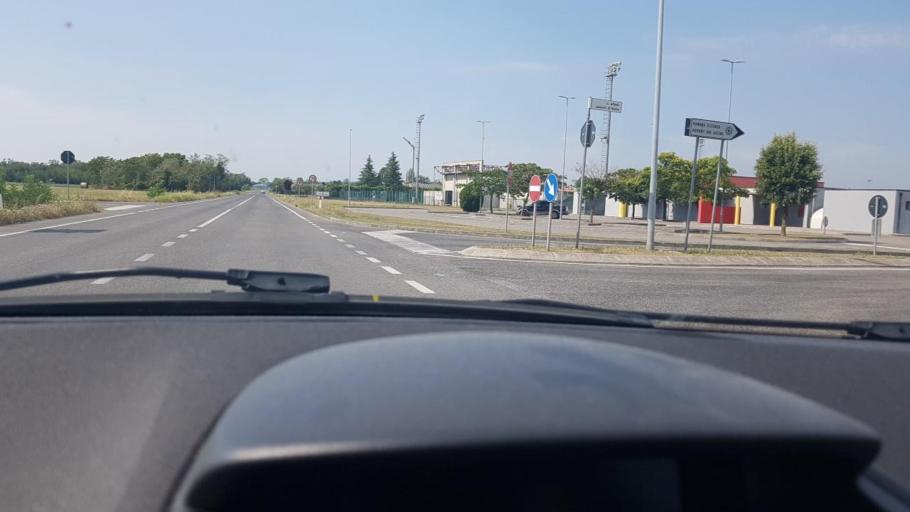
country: IT
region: Friuli Venezia Giulia
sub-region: Provincia di Gorizia
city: Romans d'Isonzo
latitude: 45.8889
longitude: 13.4320
